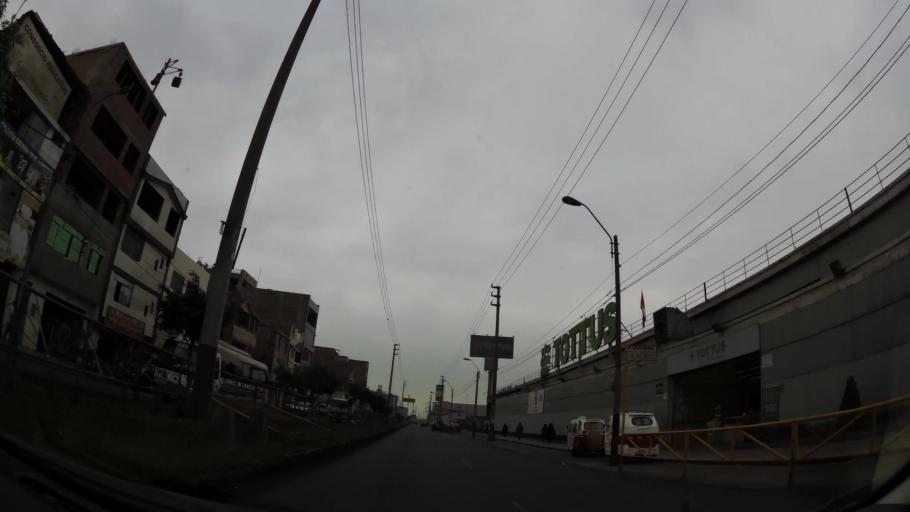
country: PE
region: Lima
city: Lima
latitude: -12.0407
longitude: -76.9998
